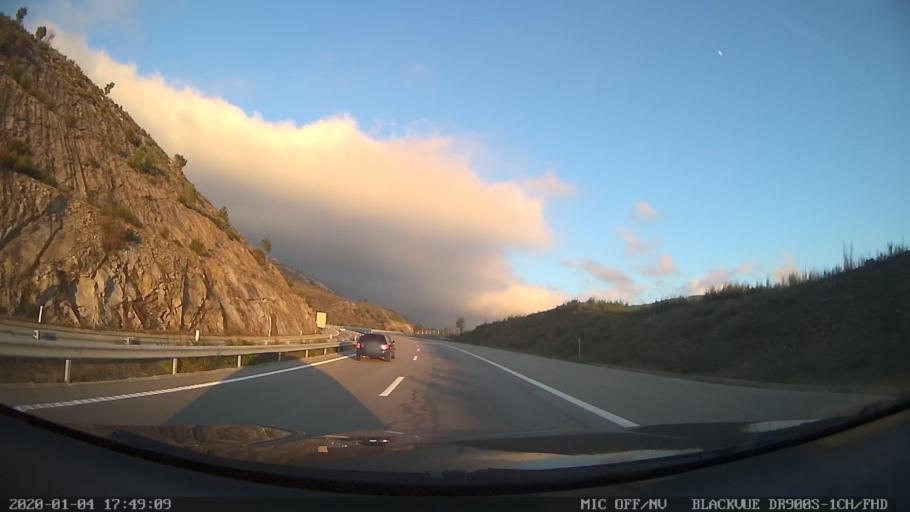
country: PT
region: Vila Real
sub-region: Ribeira de Pena
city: Ribeira de Pena
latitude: 41.4874
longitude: -7.8568
